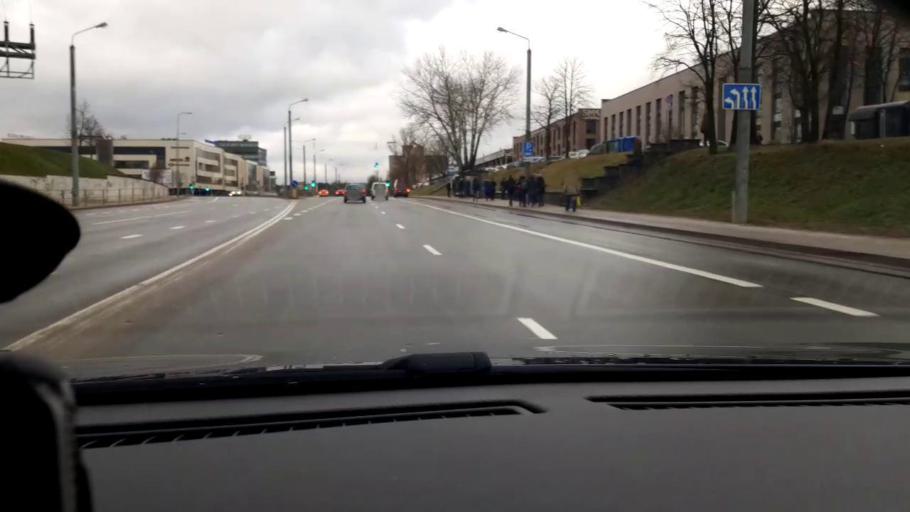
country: LT
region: Vilnius County
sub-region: Vilnius
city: Vilnius
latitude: 54.7155
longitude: 25.2869
